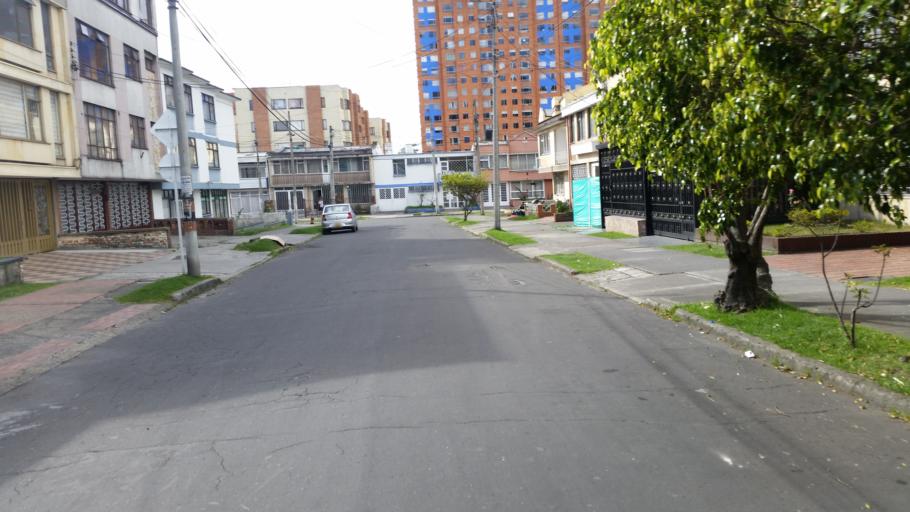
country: CO
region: Bogota D.C.
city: Bogota
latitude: 4.6274
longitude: -74.0828
